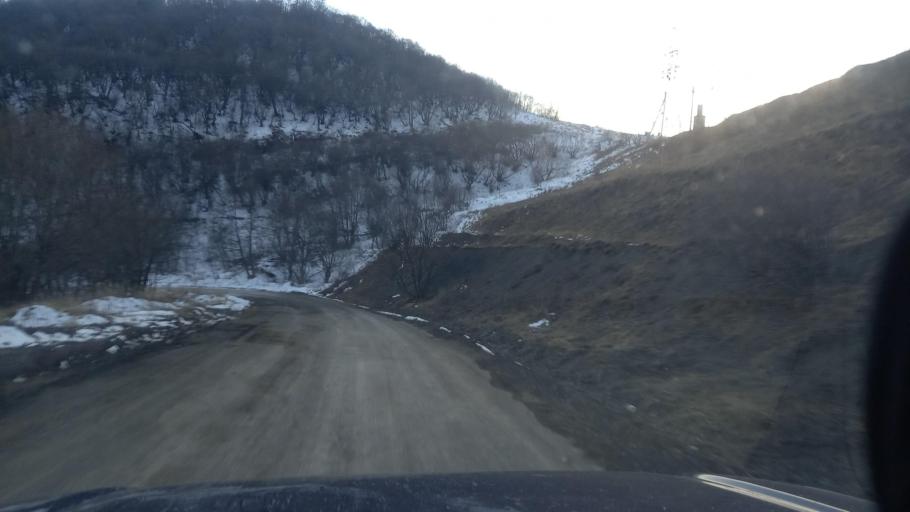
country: RU
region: Ingushetiya
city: Dzhayrakh
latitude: 42.8337
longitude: 44.5681
